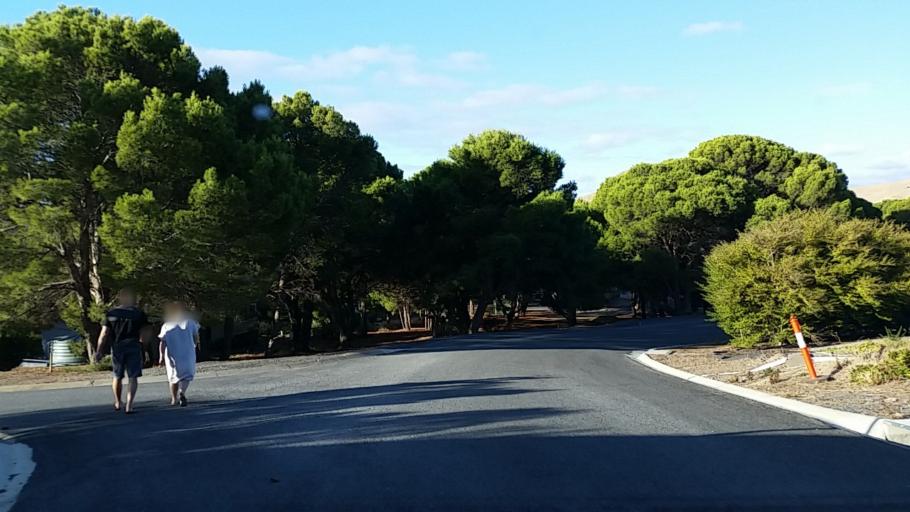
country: AU
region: South Australia
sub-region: Yankalilla
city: Normanville
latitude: -35.5147
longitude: 138.2173
